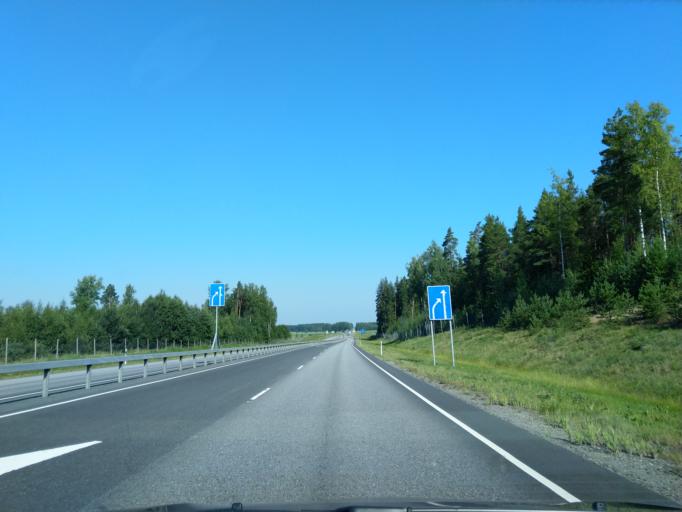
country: FI
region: Varsinais-Suomi
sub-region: Loimaa
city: Alastaro
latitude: 61.0572
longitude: 22.9465
